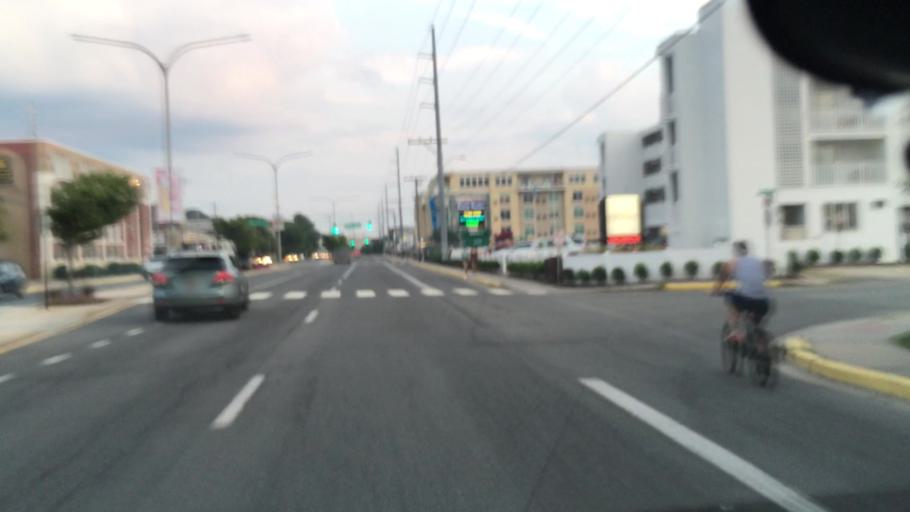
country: US
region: Delaware
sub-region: Sussex County
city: Rehoboth Beach
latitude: 38.6910
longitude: -75.0747
